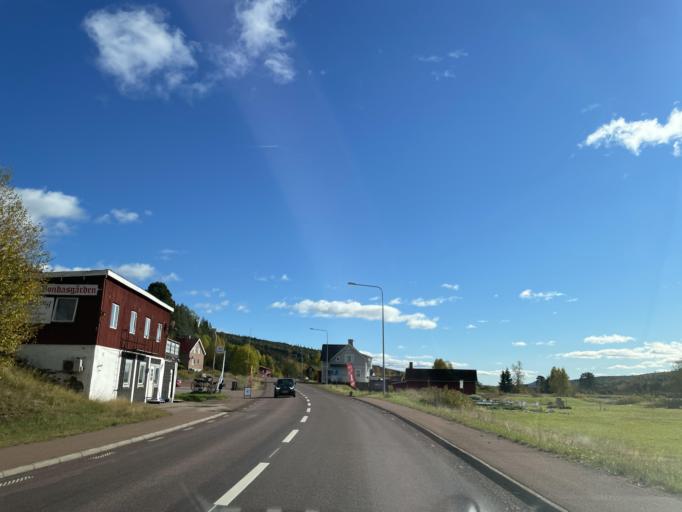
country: SE
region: Dalarna
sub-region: Malung-Saelens kommun
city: Malung
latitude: 60.9798
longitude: 13.3361
